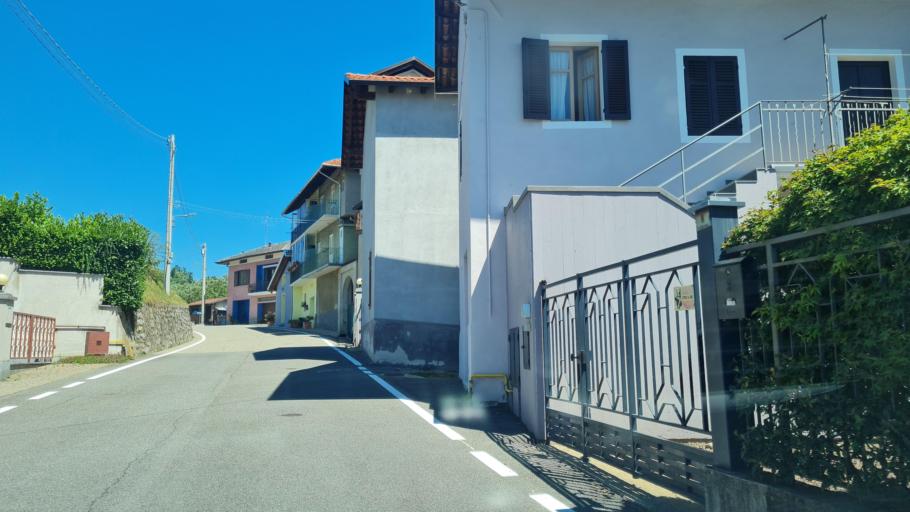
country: IT
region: Piedmont
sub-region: Provincia di Biella
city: Lessona
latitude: 45.5914
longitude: 8.2006
